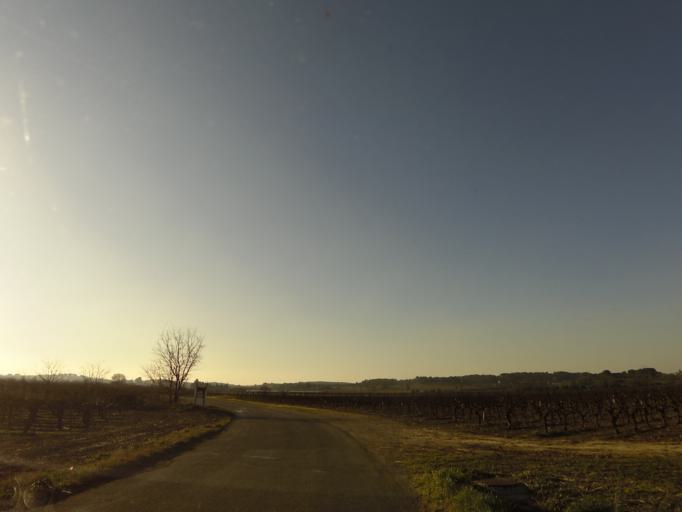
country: FR
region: Languedoc-Roussillon
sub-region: Departement du Gard
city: Mus
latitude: 43.7292
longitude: 4.2085
